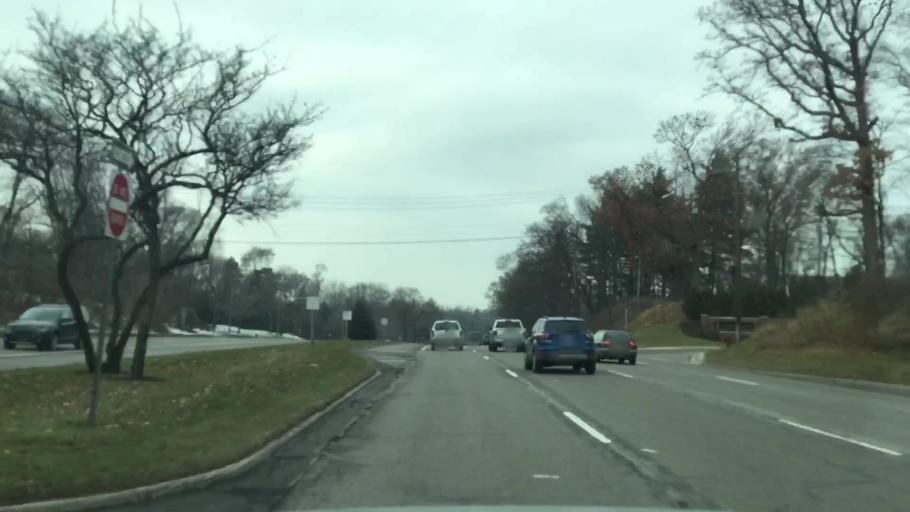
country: US
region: Michigan
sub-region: Oakland County
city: Bloomfield Hills
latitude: 42.5908
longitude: -83.2513
